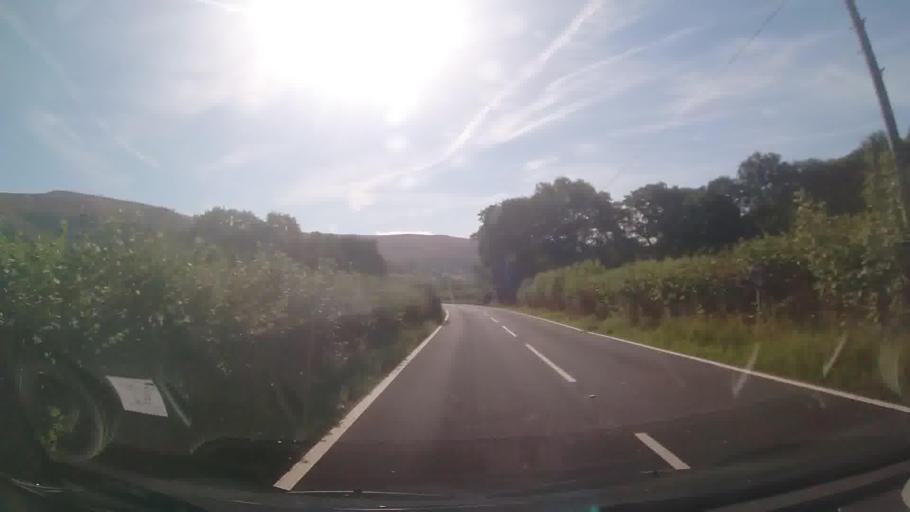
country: GB
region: Wales
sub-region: Sir Powys
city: Hay
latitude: 51.9509
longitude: -3.1936
